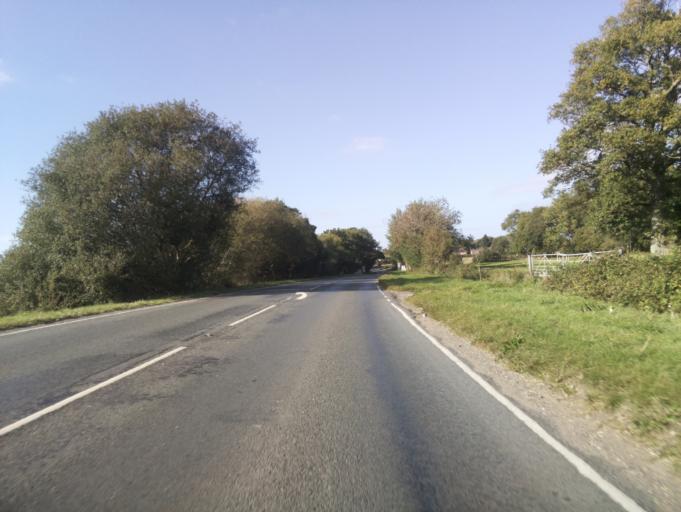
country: GB
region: England
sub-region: Hampshire
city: Tadley
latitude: 51.3181
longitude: -1.1207
